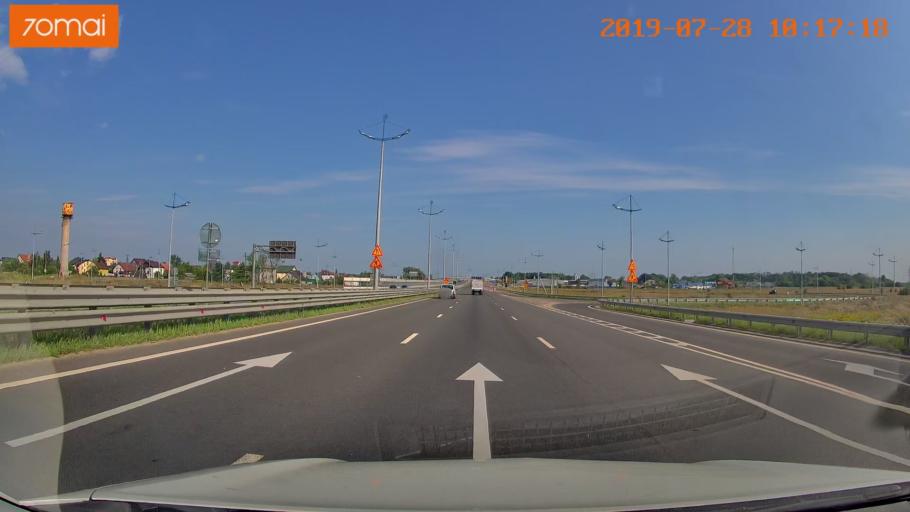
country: RU
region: Kaliningrad
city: Maloye Isakovo
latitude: 54.7381
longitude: 20.5952
